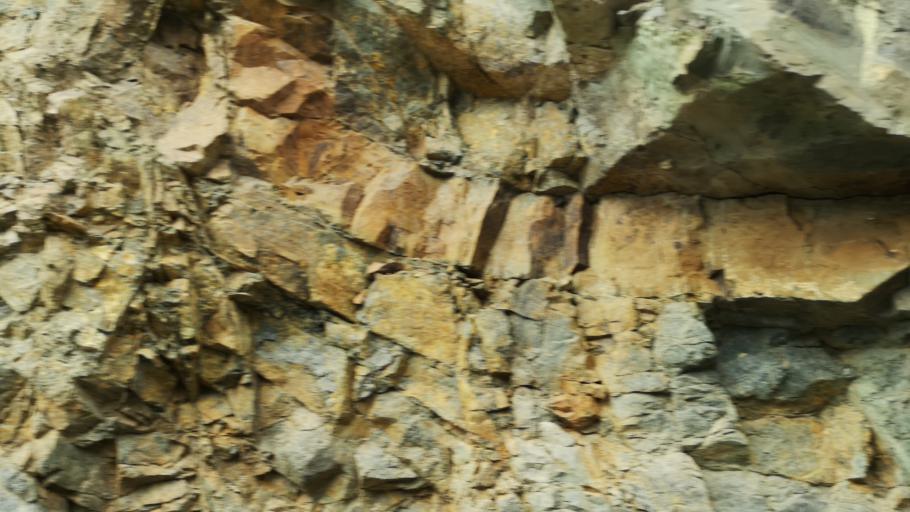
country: ES
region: Canary Islands
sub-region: Provincia de Santa Cruz de Tenerife
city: Vallehermosa
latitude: 28.1959
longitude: -17.2583
